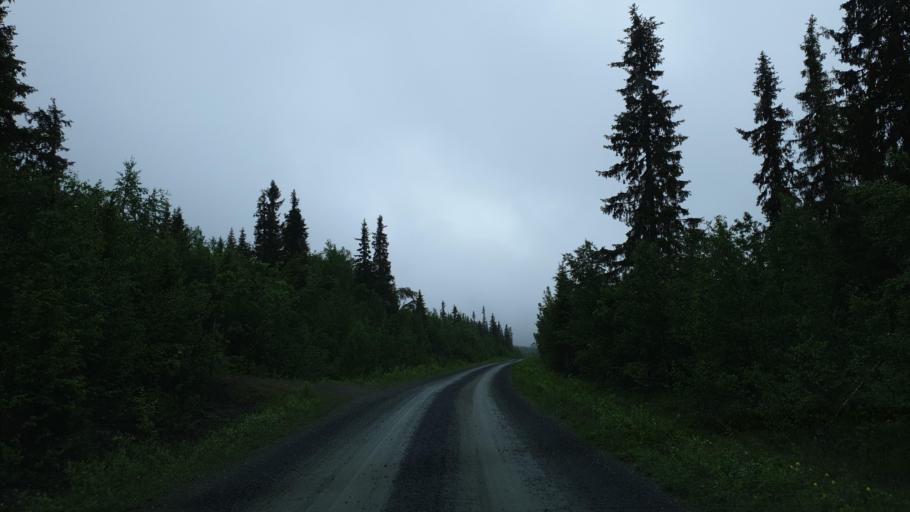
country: SE
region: Vaesterbotten
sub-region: Vilhelmina Kommun
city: Sjoberg
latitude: 65.3263
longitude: 15.9263
